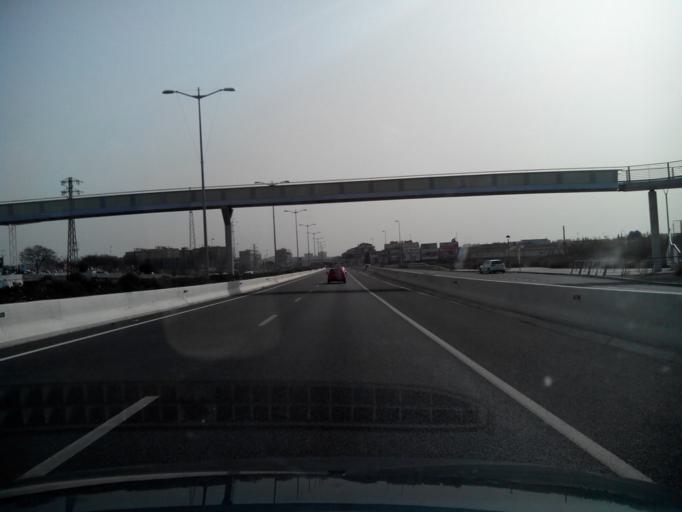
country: ES
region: Catalonia
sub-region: Provincia de Tarragona
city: Constanti
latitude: 41.1268
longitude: 1.2054
